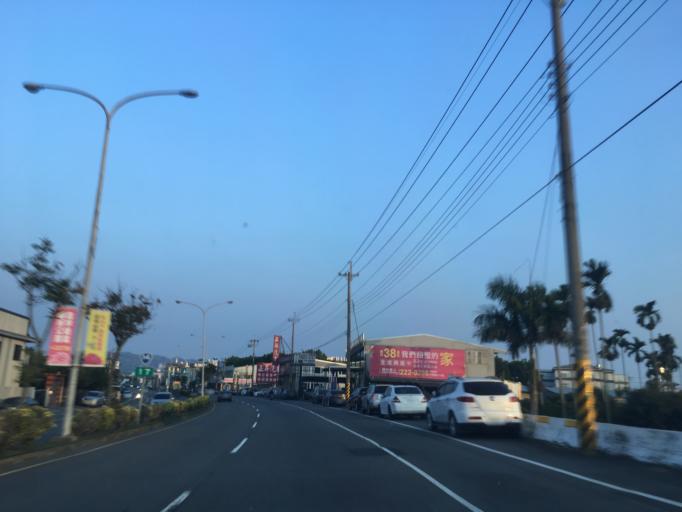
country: TW
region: Taiwan
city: Zhongxing New Village
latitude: 23.9923
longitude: 120.6668
